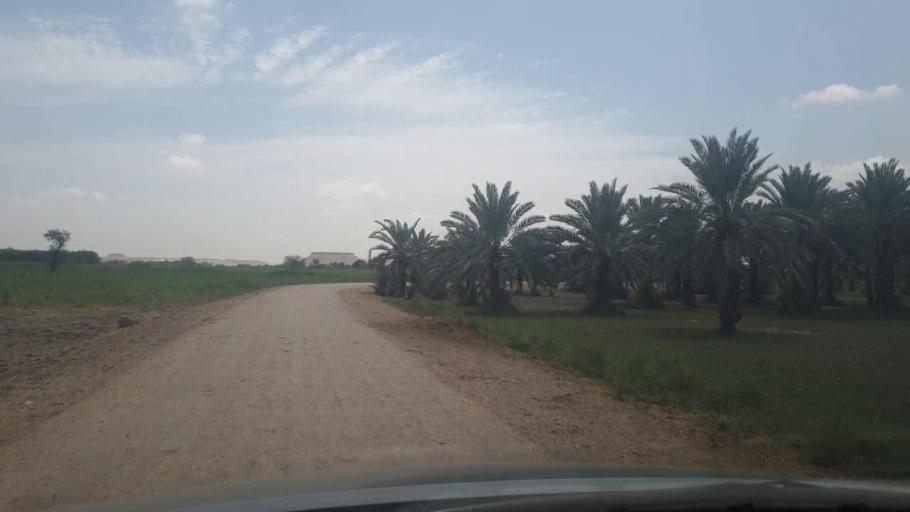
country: PK
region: Sindh
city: Kot Diji
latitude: 27.3943
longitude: 68.7619
